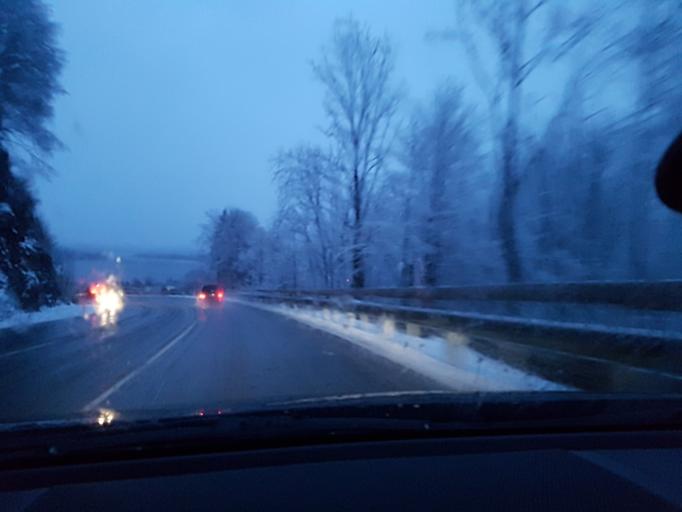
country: AT
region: Salzburg
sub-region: Politischer Bezirk Salzburg-Umgebung
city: Sankt Gilgen
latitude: 47.7728
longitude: 13.3505
